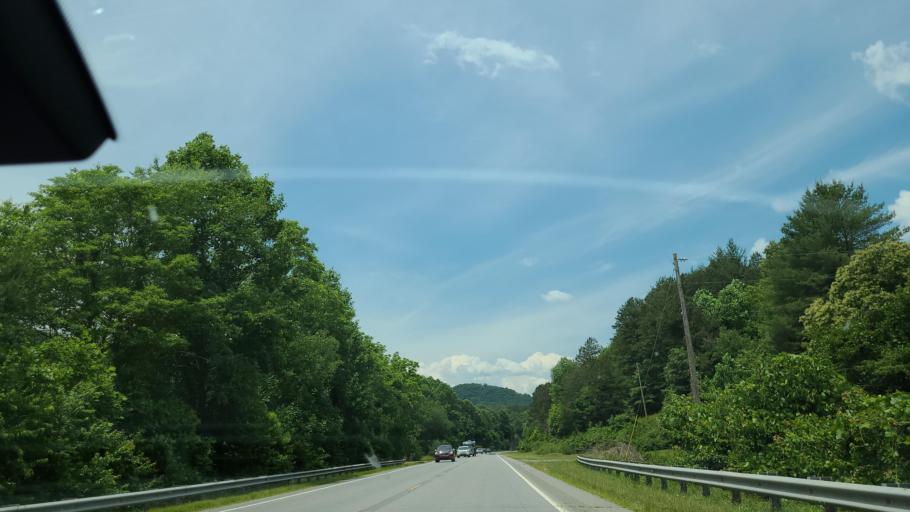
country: US
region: Georgia
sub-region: Towns County
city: Hiawassee
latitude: 35.0233
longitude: -83.6878
